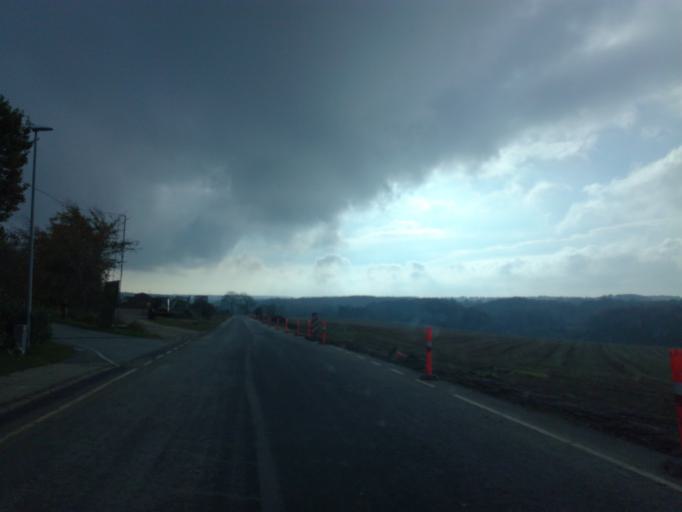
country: DK
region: South Denmark
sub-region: Vejle Kommune
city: Vejle
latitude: 55.6697
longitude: 9.5759
